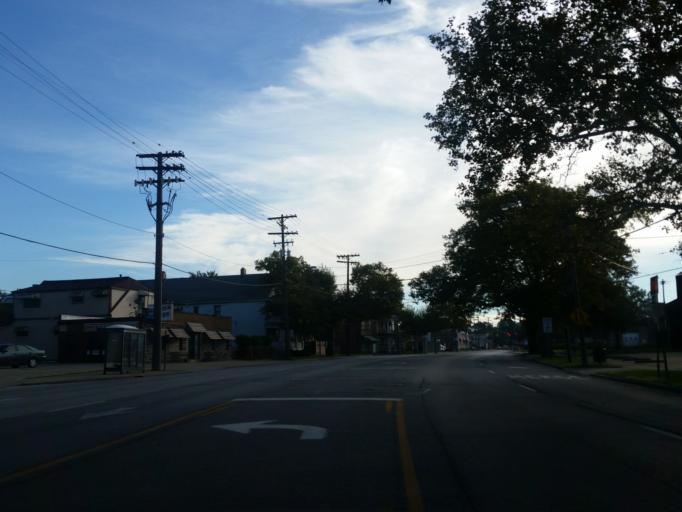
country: US
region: Ohio
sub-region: Cuyahoga County
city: Newburgh Heights
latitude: 41.4481
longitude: -81.6544
